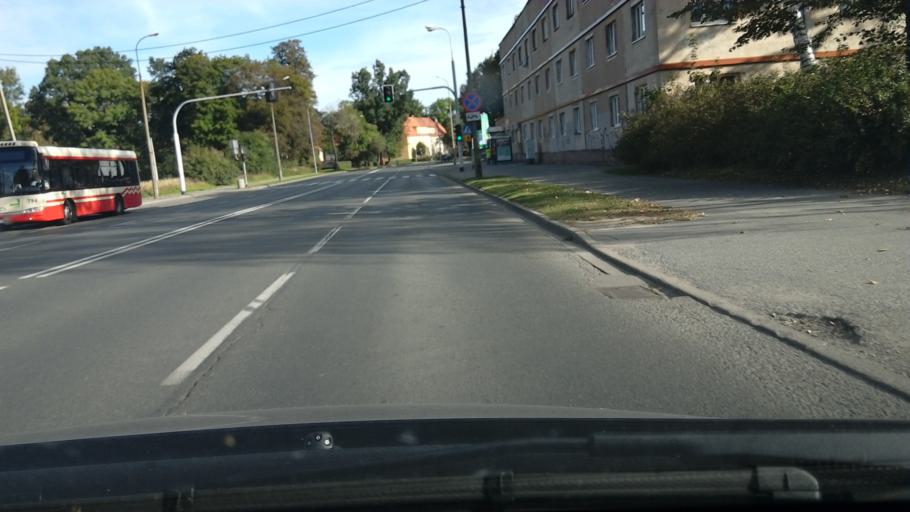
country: PL
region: Lower Silesian Voivodeship
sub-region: Jelenia Gora
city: Jelenia Gora
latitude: 50.8881
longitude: 15.7197
